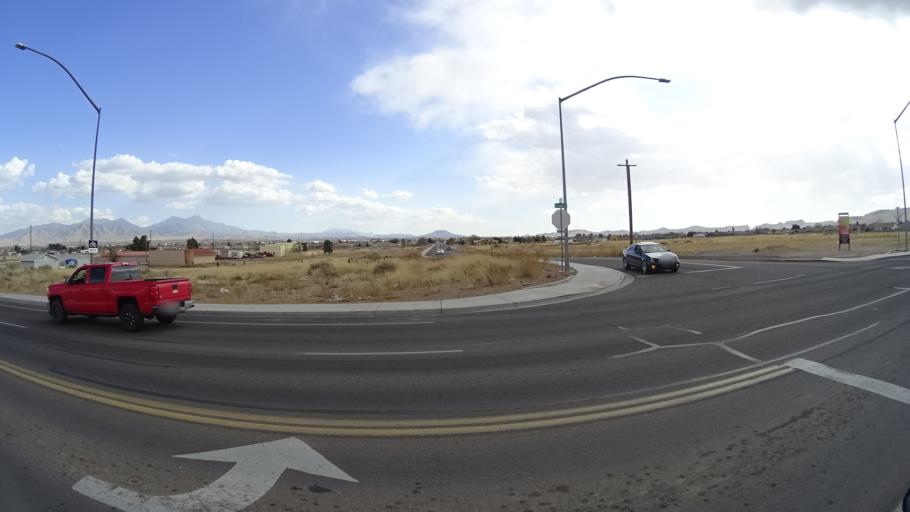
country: US
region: Arizona
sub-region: Mohave County
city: New Kingman-Butler
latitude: 35.2396
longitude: -114.0247
